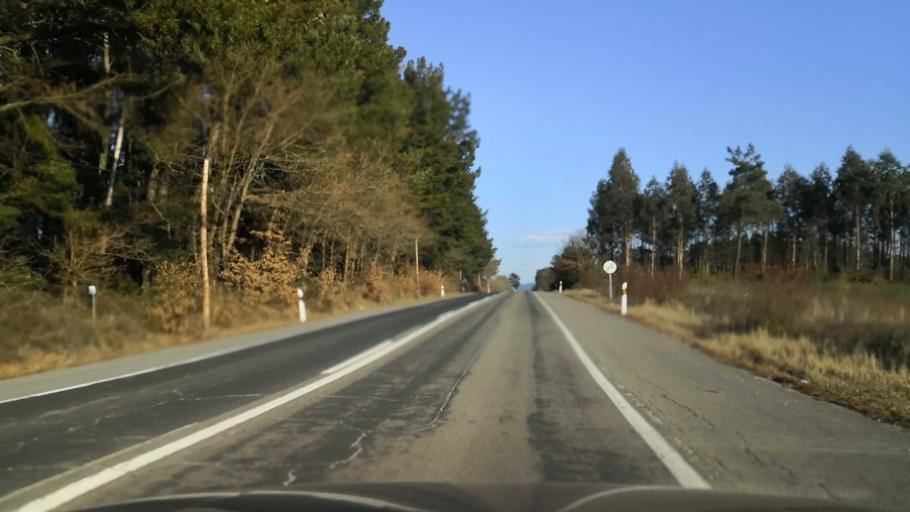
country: ES
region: Galicia
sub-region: Provincia de Lugo
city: Corgo
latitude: 42.9380
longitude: -7.4148
